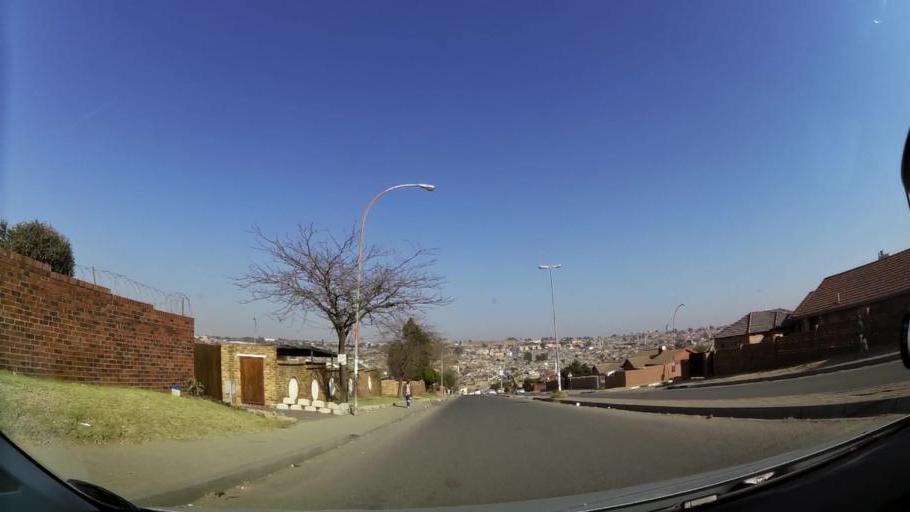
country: ZA
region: Gauteng
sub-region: City of Johannesburg Metropolitan Municipality
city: Modderfontein
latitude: -26.1042
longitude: 28.1119
